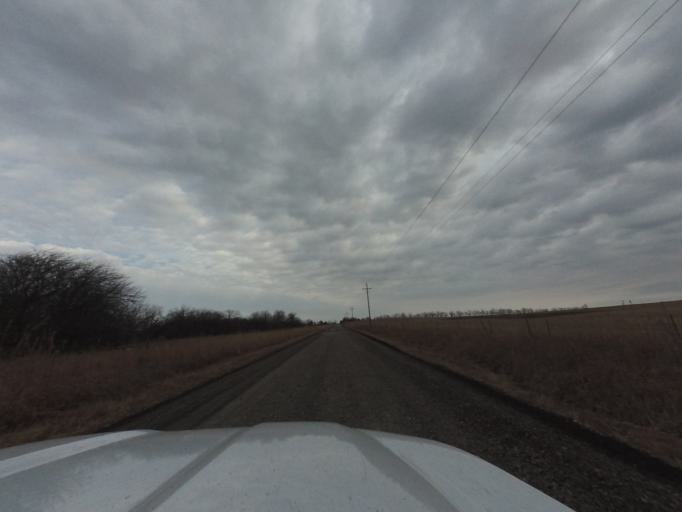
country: US
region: Kansas
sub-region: Chase County
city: Cottonwood Falls
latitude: 38.4345
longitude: -96.3731
